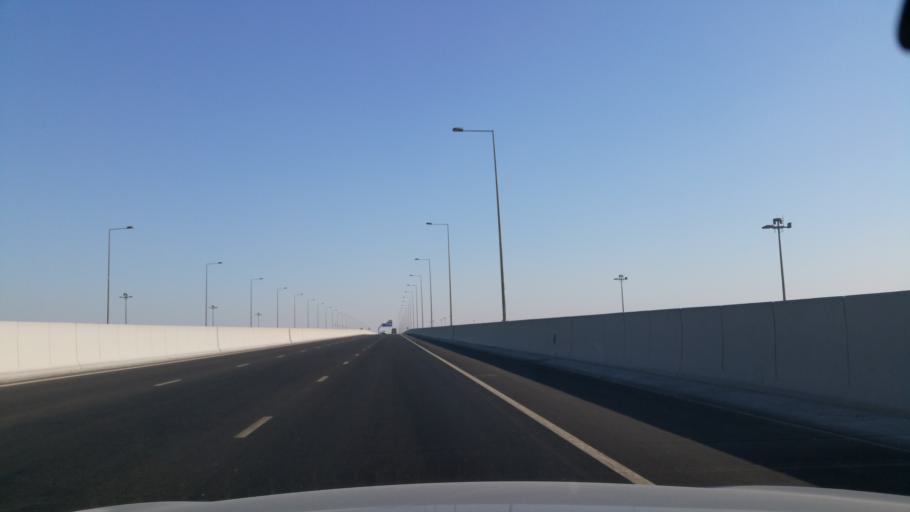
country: QA
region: Al Wakrah
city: Al Wukayr
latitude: 25.1838
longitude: 51.4618
